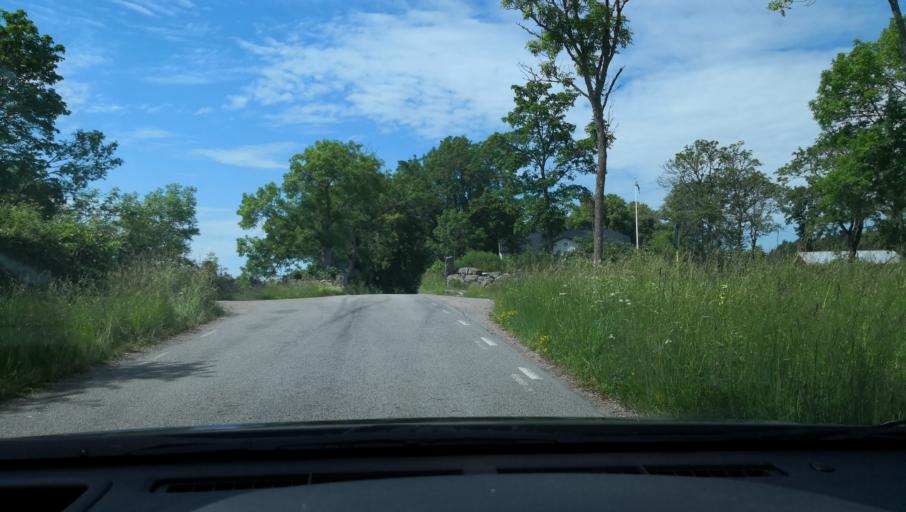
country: SE
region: Stockholm
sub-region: Sigtuna Kommun
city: Sigtuna
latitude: 59.6786
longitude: 17.6951
